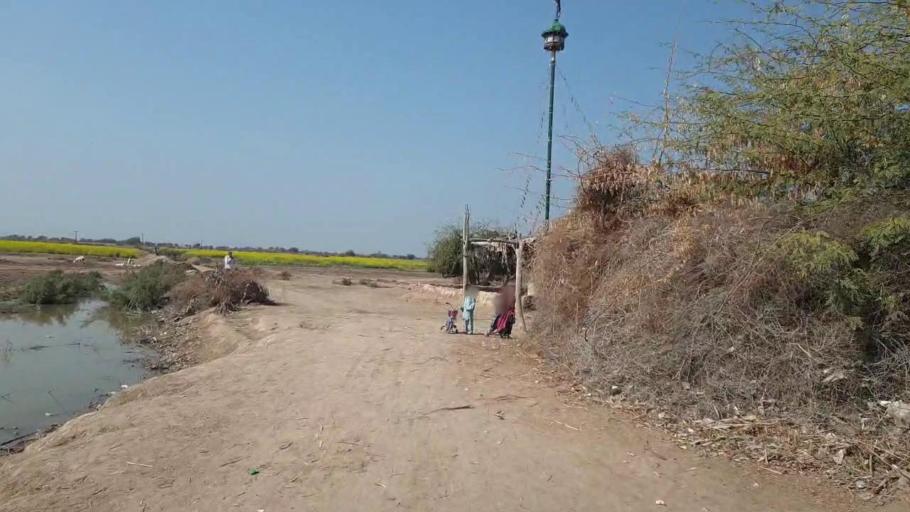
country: PK
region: Sindh
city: Hala
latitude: 25.9480
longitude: 68.4333
